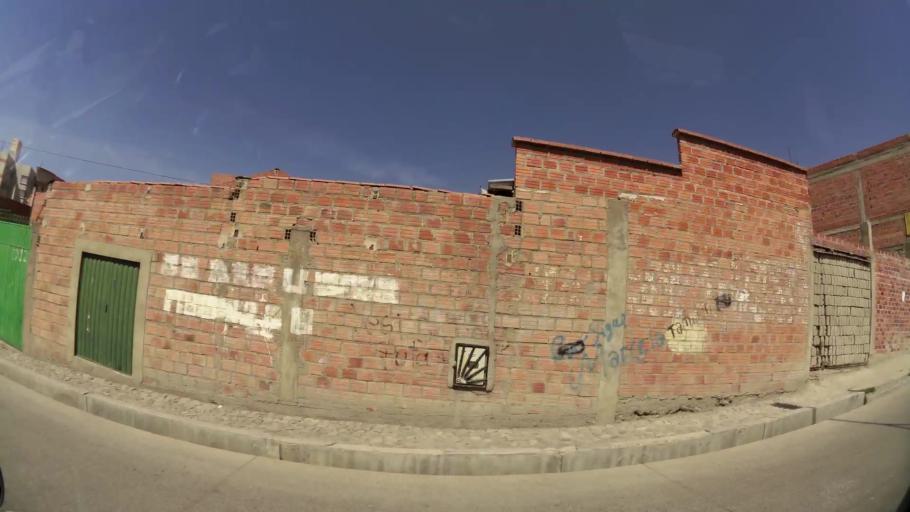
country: BO
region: La Paz
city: La Paz
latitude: -16.5262
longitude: -68.1264
